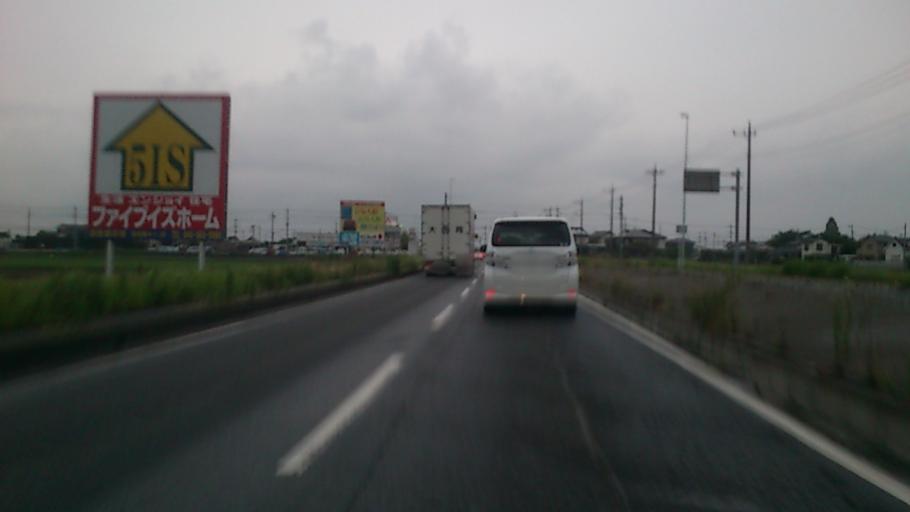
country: JP
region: Saitama
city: Hanyu
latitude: 36.1510
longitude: 139.5303
